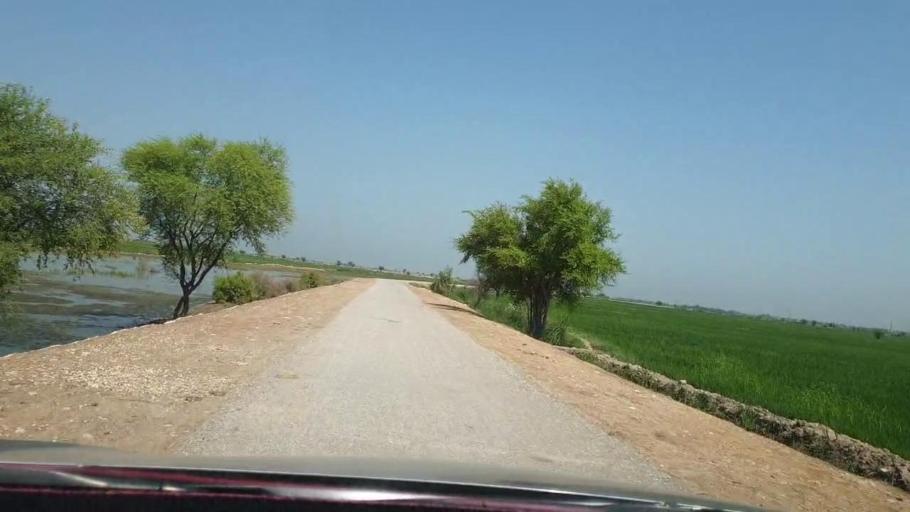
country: PK
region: Sindh
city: Warah
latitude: 27.5619
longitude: 67.7411
